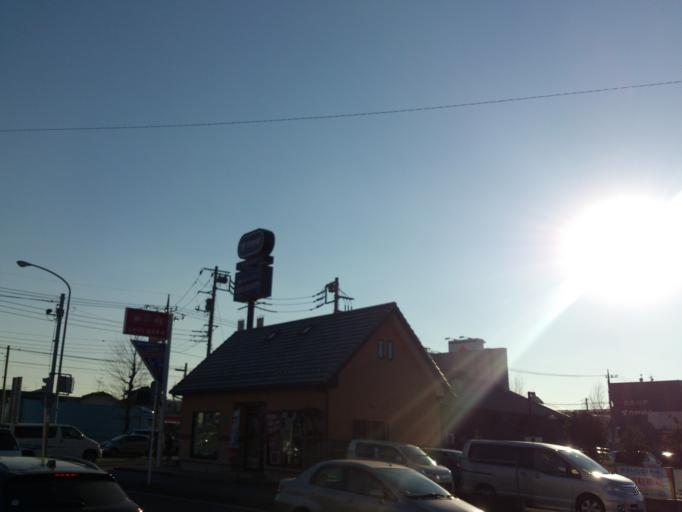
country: JP
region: Chiba
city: Kashiwa
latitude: 35.7960
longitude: 139.9645
